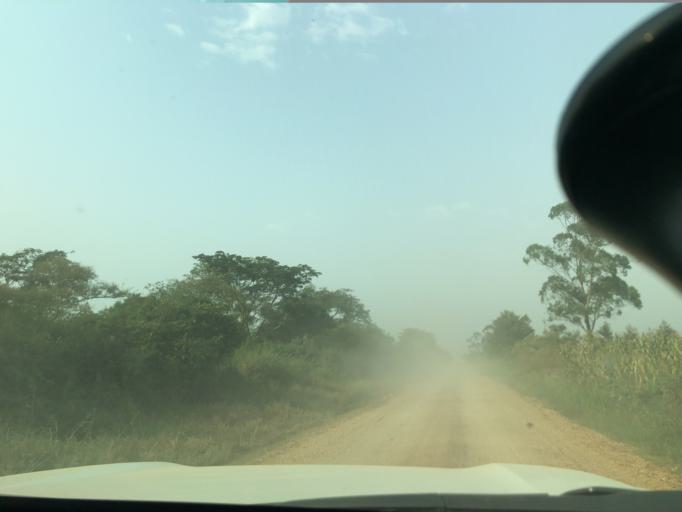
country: CD
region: Nord Kivu
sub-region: North Kivu
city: Butembo
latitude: 0.1609
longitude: 29.6447
